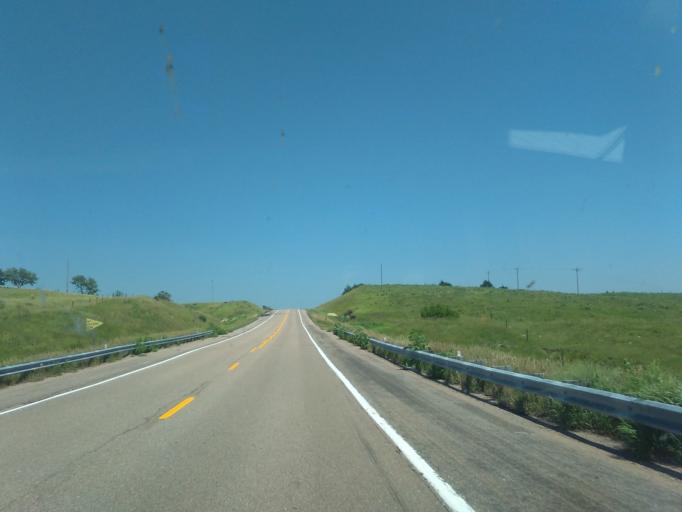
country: US
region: Nebraska
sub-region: Frontier County
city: Stockville
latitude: 40.5855
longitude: -100.6295
